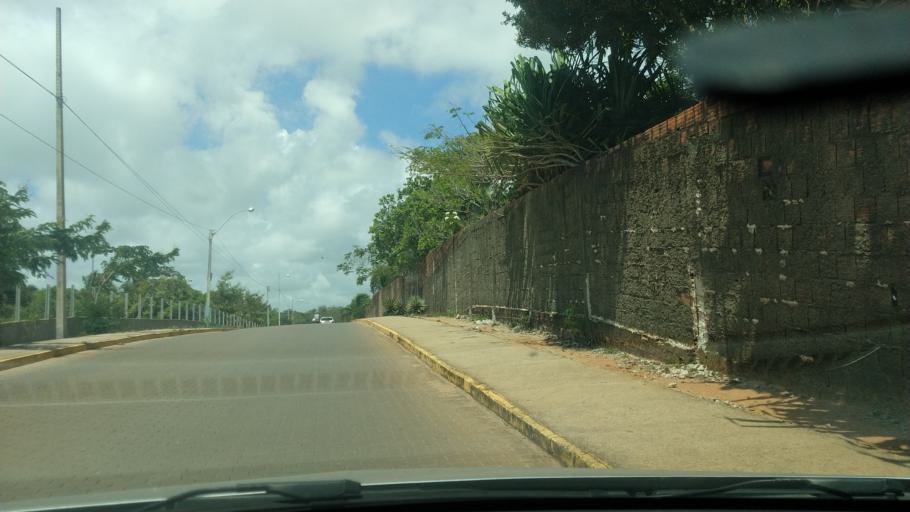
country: BR
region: Rio Grande do Norte
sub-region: Ares
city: Ares
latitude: -6.2340
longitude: -35.0479
